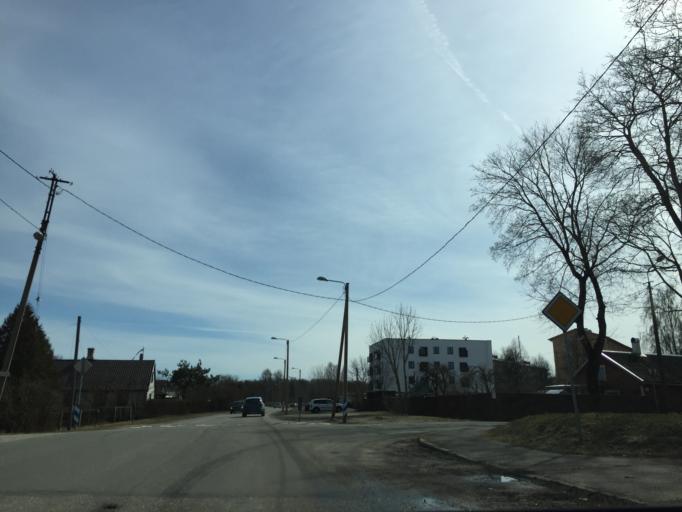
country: EE
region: Paernumaa
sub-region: Paernu linn
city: Parnu
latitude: 58.3822
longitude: 24.5290
